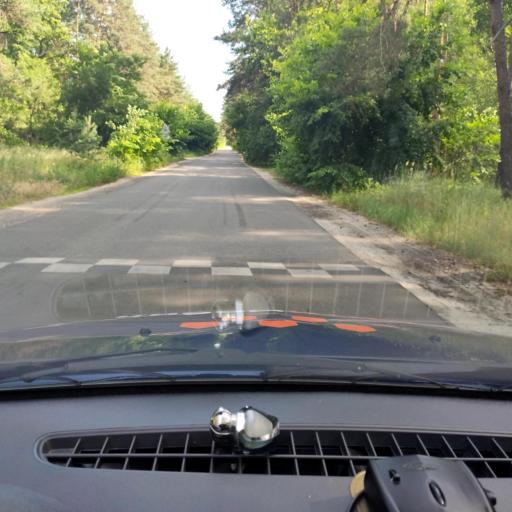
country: RU
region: Voronezj
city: Somovo
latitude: 51.7636
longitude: 39.3655
